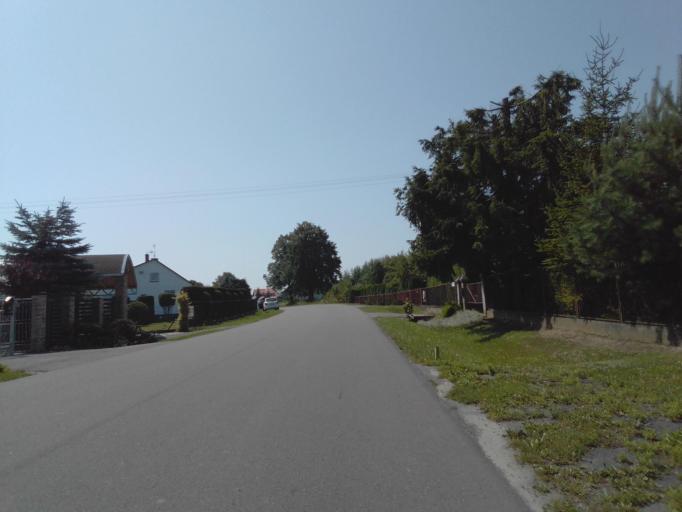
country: PL
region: Subcarpathian Voivodeship
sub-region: Powiat ropczycko-sedziszowski
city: Sedziszow Malopolski
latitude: 50.0654
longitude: 21.6634
